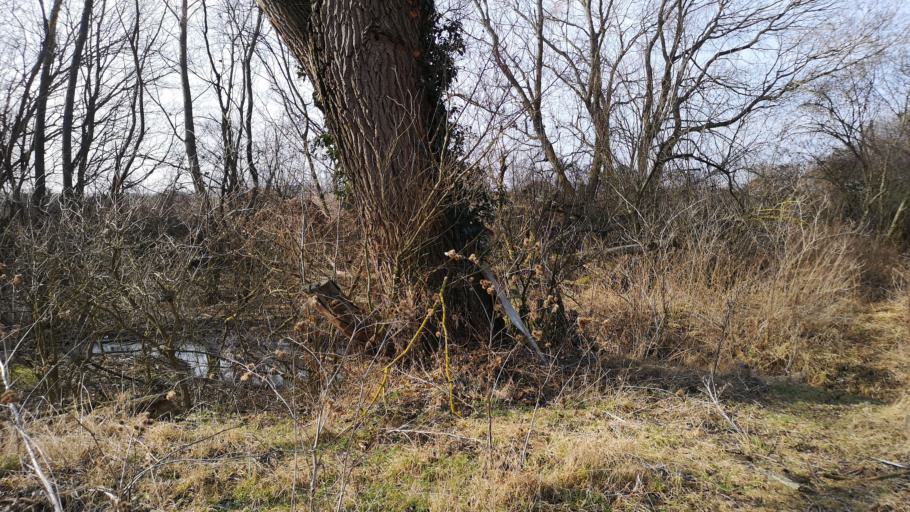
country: SK
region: Nitriansky
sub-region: Okres Nitra
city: Nitra
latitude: 48.2839
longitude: 18.0319
